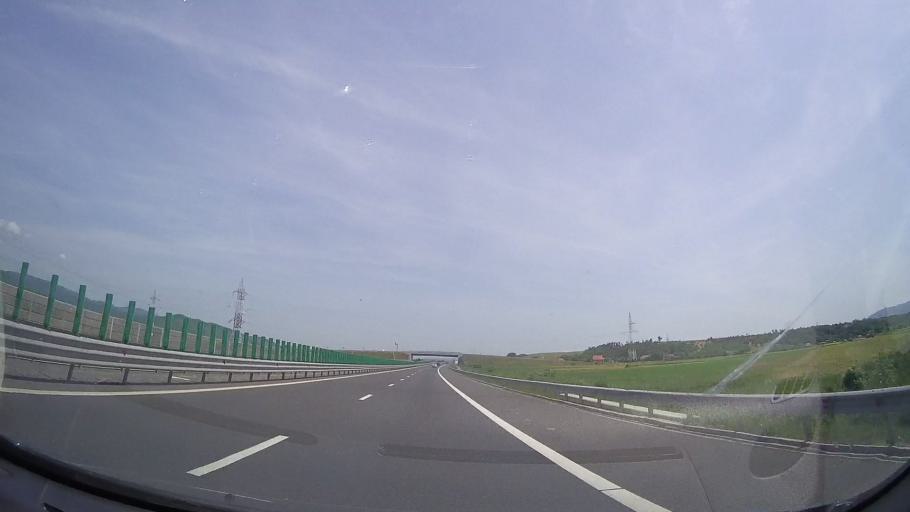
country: RO
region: Alba
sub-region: Comuna Sibot
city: Sibot
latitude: 45.9209
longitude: 23.3364
